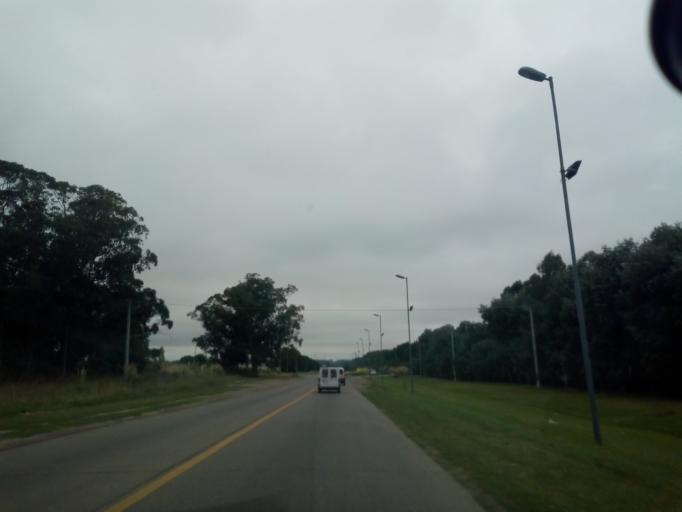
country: AR
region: Buenos Aires
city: Mar del Plata
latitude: -38.0778
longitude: -57.5819
